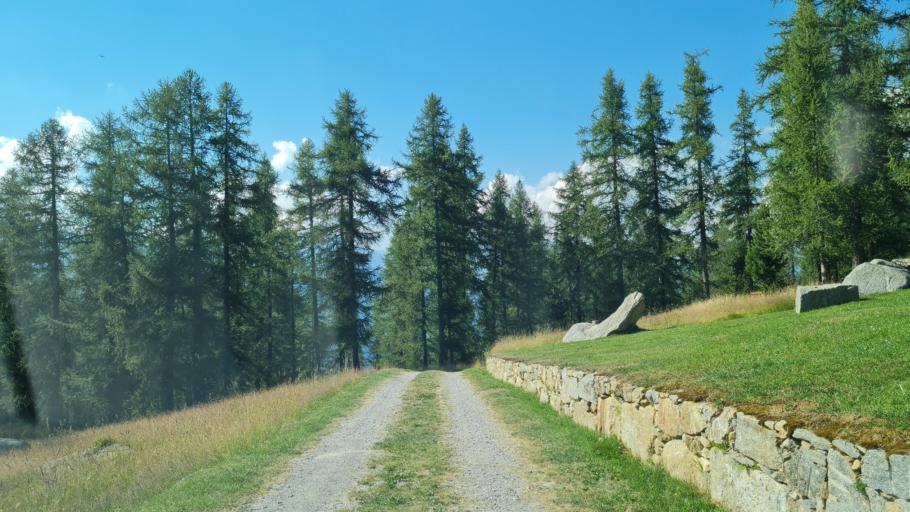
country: IT
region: Aosta Valley
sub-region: Valle d'Aosta
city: Fontainemore
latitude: 45.6232
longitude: 7.8742
